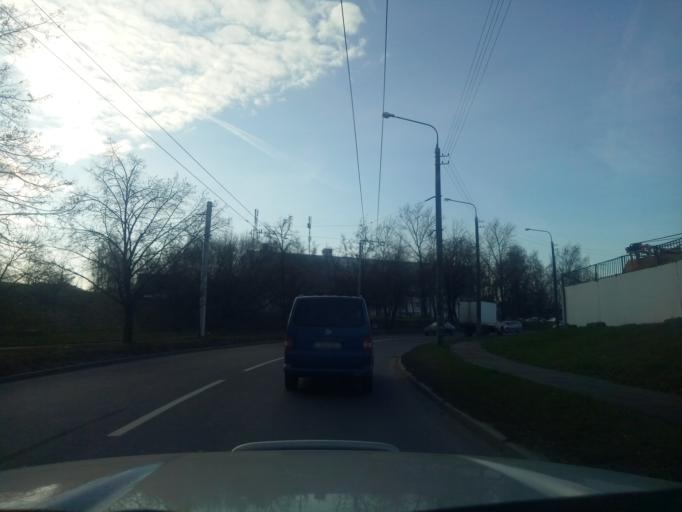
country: BY
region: Minsk
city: Novoye Medvezhino
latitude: 53.8851
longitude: 27.4981
